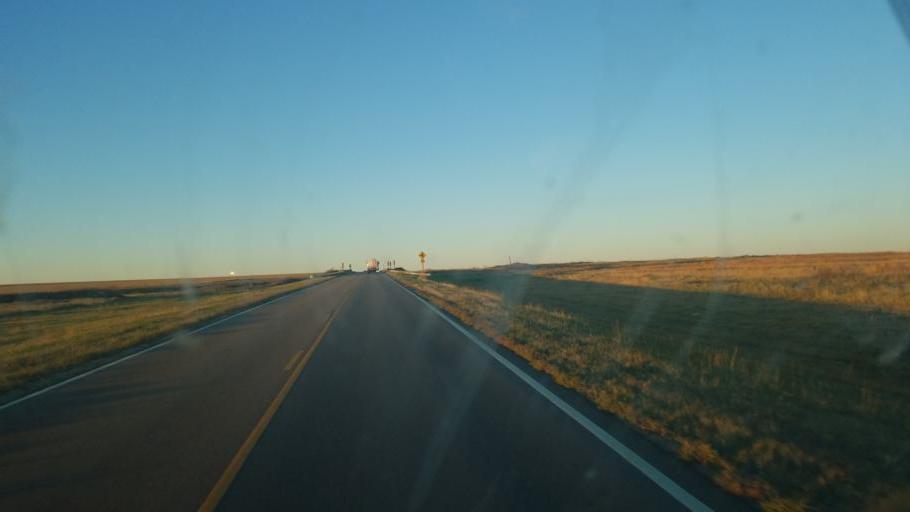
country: US
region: Kansas
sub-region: Wallace County
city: Sharon Springs
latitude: 38.8932
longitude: -101.8710
